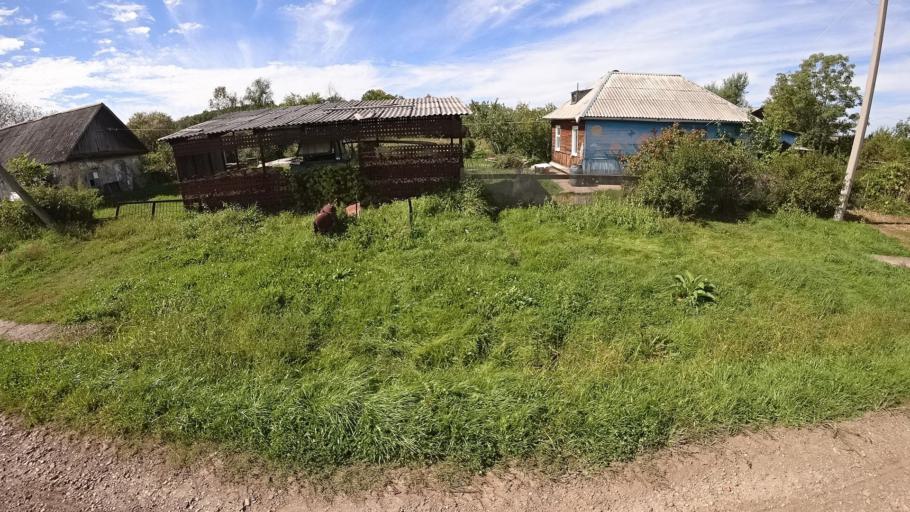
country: RU
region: Primorskiy
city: Yakovlevka
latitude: 44.4294
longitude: 133.5605
